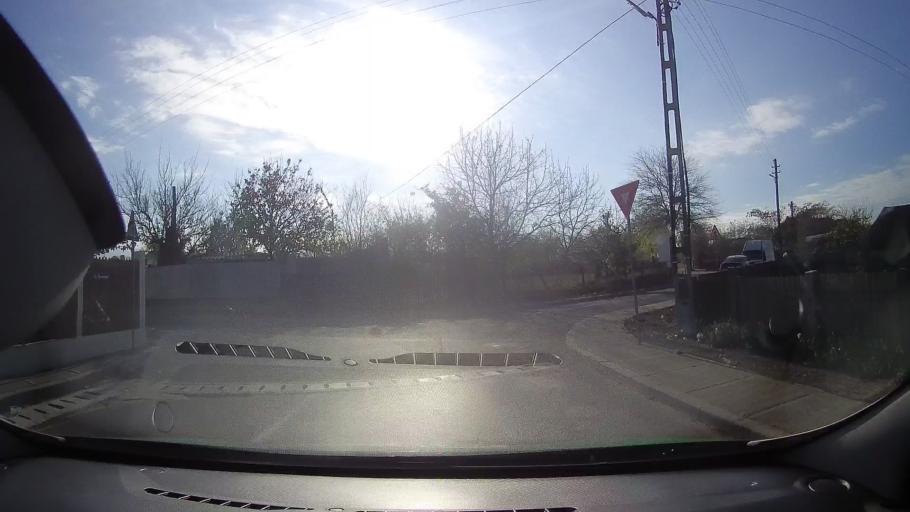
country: RO
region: Tulcea
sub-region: Comuna Murighiol
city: Murighiol
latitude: 45.0370
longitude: 29.1667
